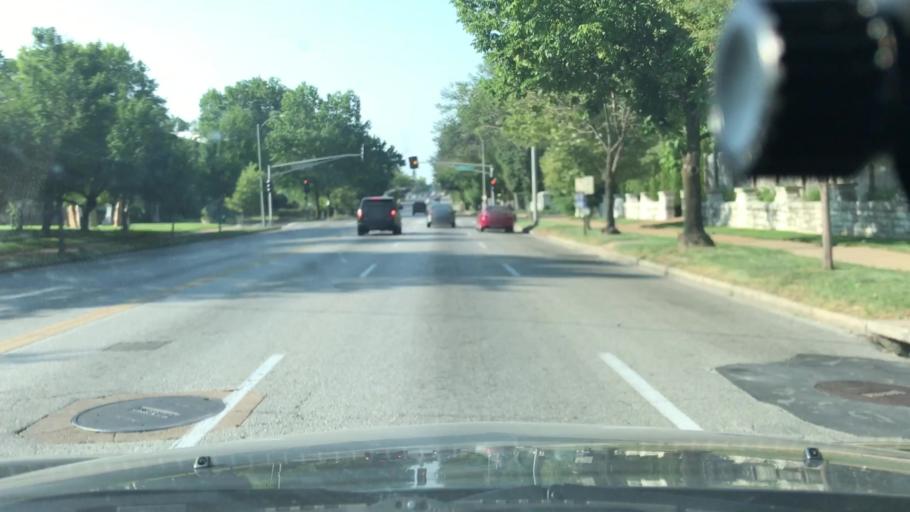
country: US
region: Missouri
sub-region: Saint Louis County
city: Hillsdale
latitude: 38.6474
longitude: -90.2642
